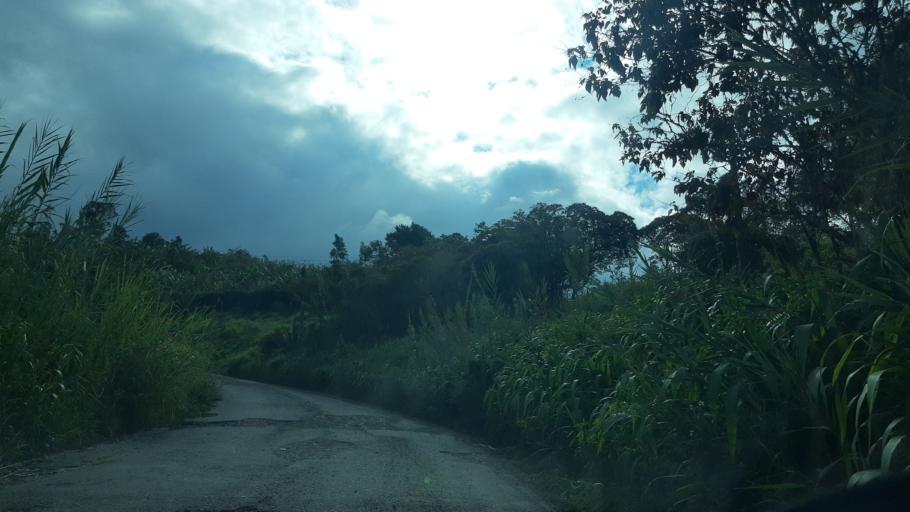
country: CO
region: Cundinamarca
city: Tenza
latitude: 5.0540
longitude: -73.4171
